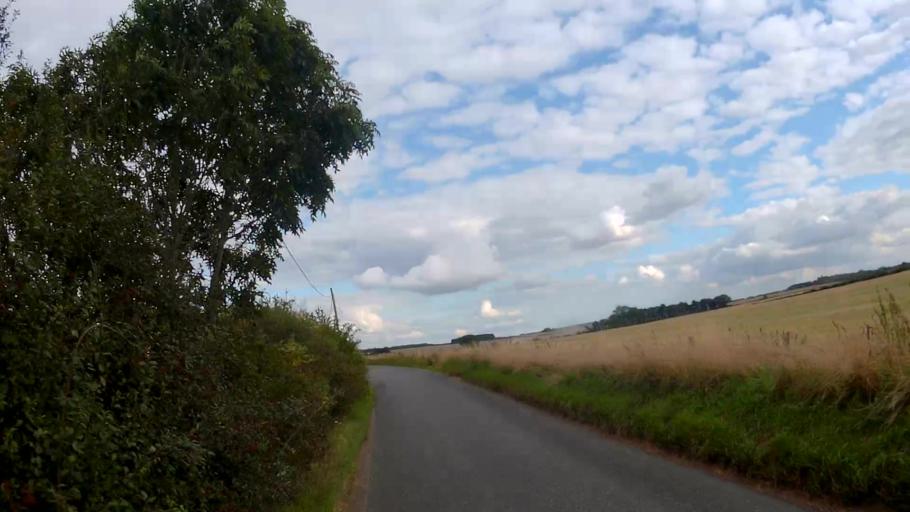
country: GB
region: England
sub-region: Hampshire
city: Kings Worthy
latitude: 51.1517
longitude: -1.3155
